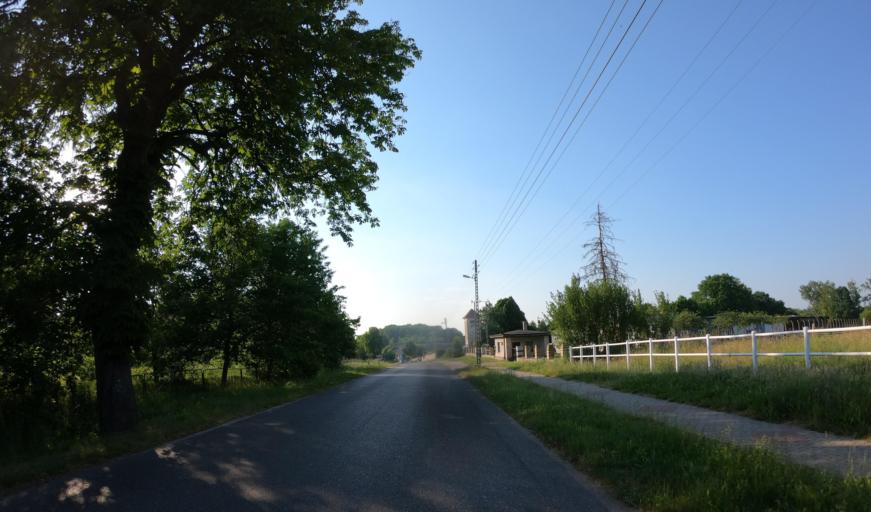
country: PL
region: West Pomeranian Voivodeship
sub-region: Powiat lobeski
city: Resko
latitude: 53.7639
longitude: 15.4063
